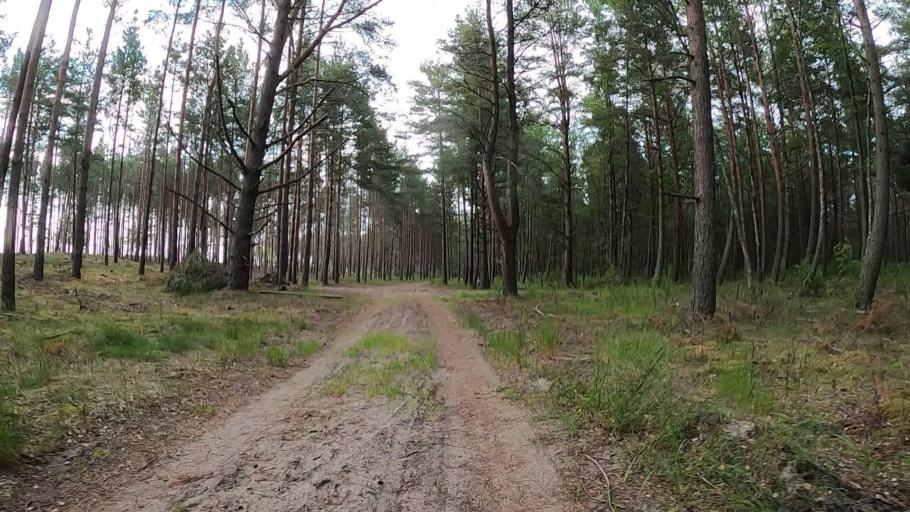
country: LV
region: Carnikava
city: Carnikava
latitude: 57.1490
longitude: 24.2510
